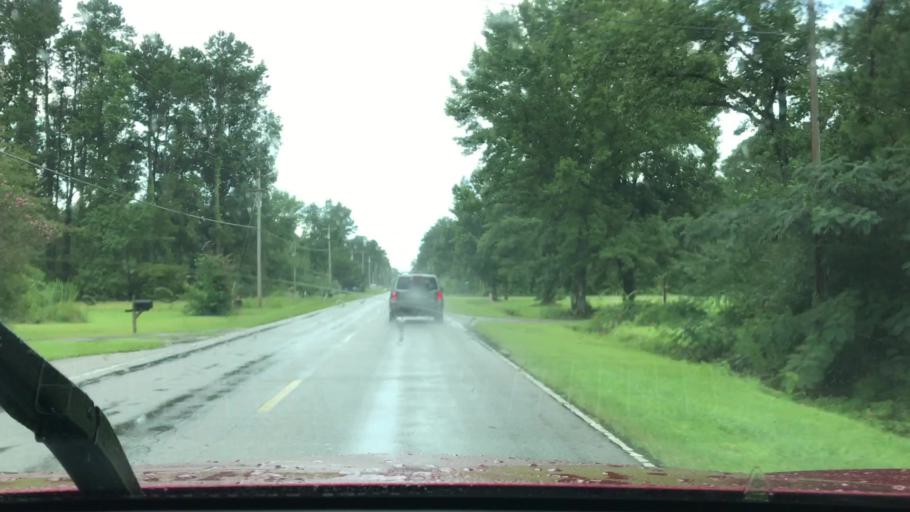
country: US
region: South Carolina
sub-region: Horry County
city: Red Hill
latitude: 33.8563
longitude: -79.0050
